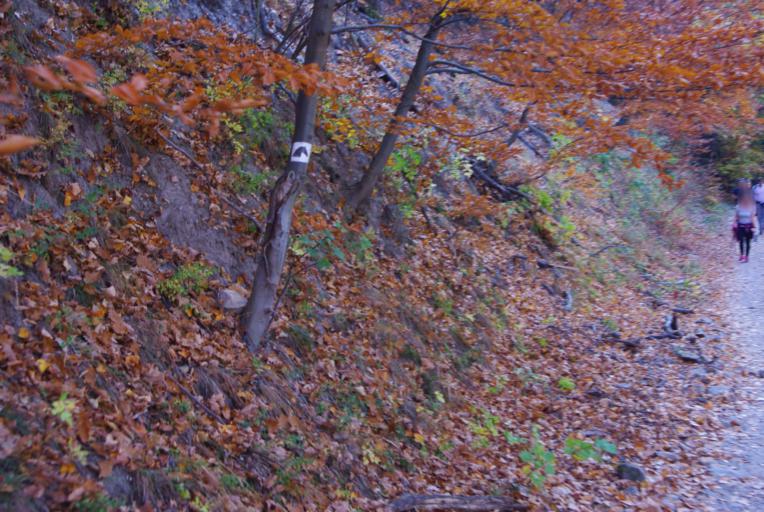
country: HU
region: Pest
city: Pilisszentkereszt
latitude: 47.7379
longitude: 18.9276
